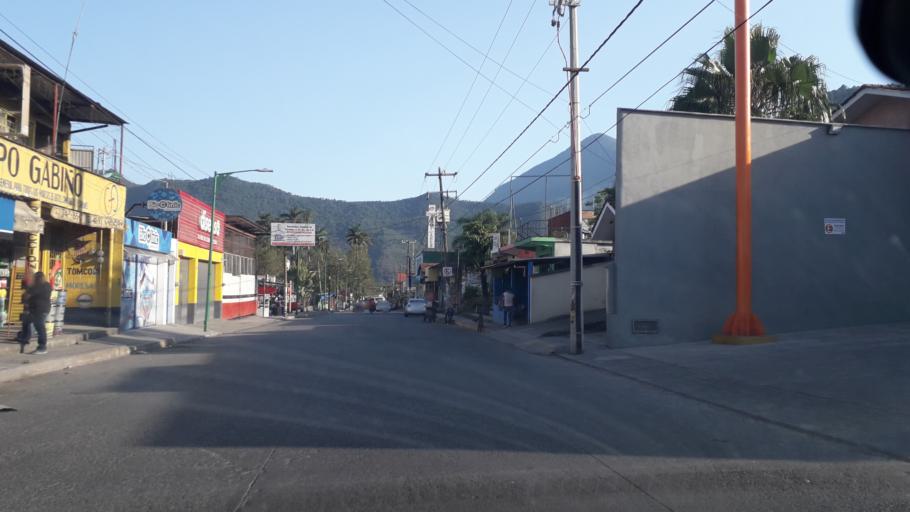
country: MX
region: Veracruz
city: Jalapilla
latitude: 18.8252
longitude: -97.0899
